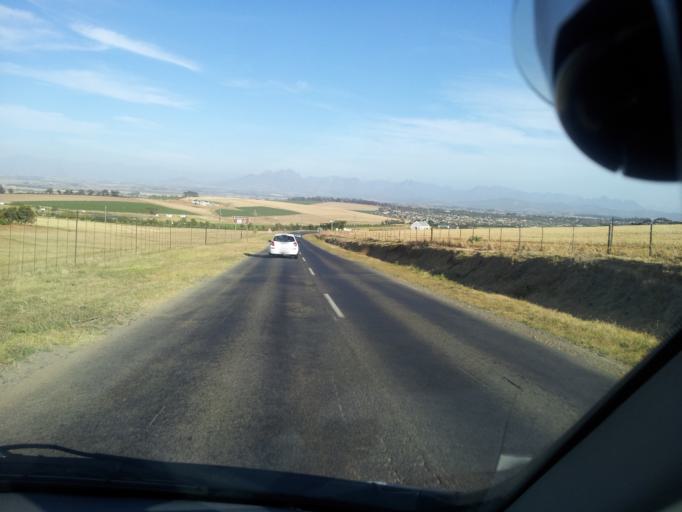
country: ZA
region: Western Cape
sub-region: City of Cape Town
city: Kraaifontein
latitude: -33.8011
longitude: 18.6157
